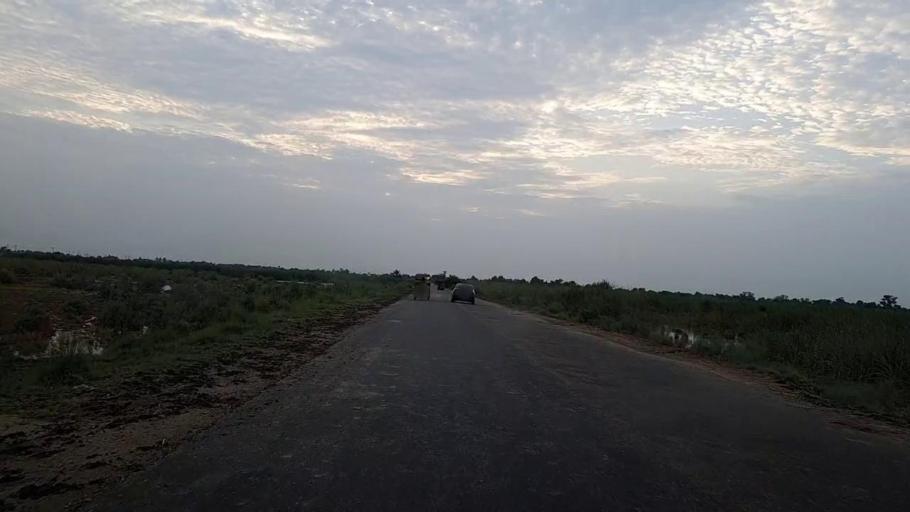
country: PK
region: Sindh
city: Naushahro Firoz
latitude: 26.8145
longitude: 68.1860
